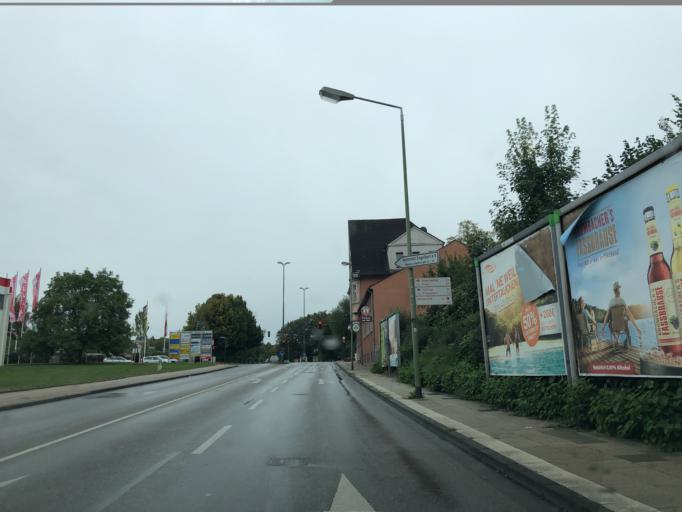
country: DE
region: North Rhine-Westphalia
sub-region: Regierungsbezirk Dusseldorf
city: Essen
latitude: 51.4706
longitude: 7.0447
